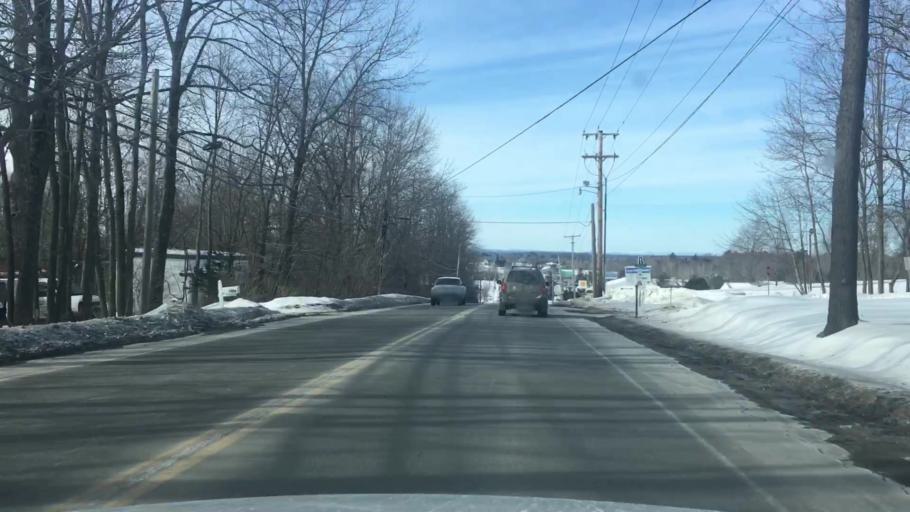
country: US
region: Maine
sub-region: Penobscot County
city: Bangor
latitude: 44.8326
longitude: -68.7880
